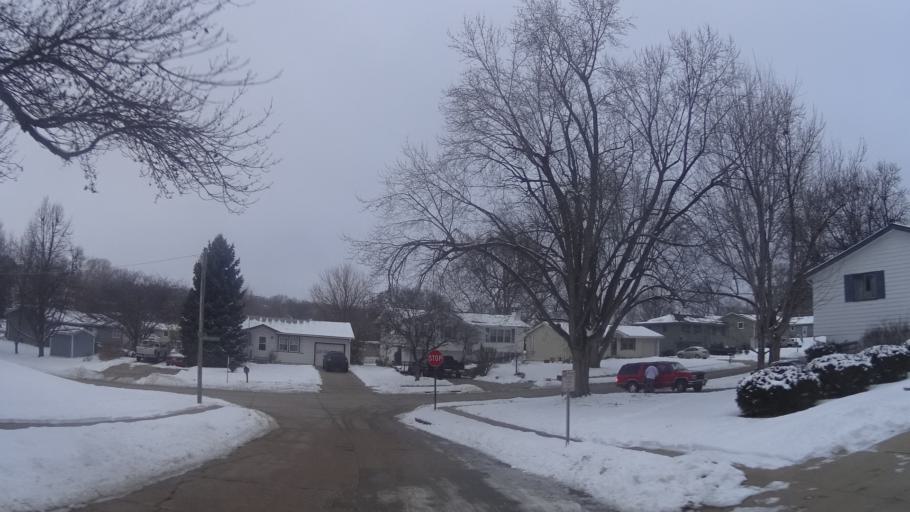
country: US
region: Nebraska
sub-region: Sarpy County
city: Offutt Air Force Base
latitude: 41.1420
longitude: -95.9193
